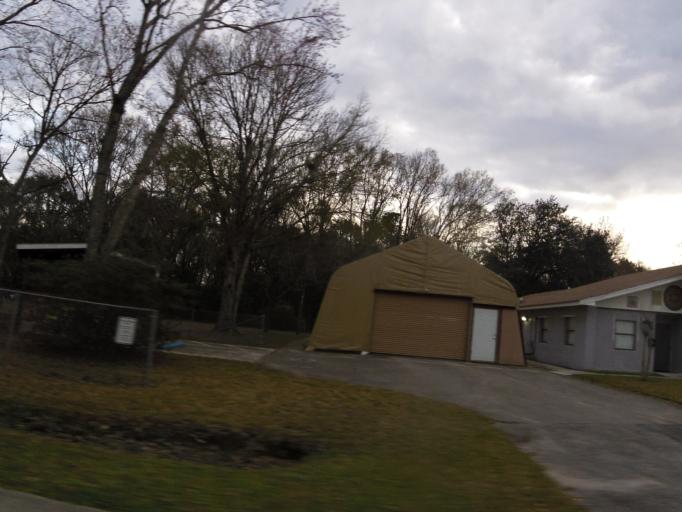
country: US
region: Florida
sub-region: Duval County
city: Baldwin
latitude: 30.3010
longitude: -81.9799
